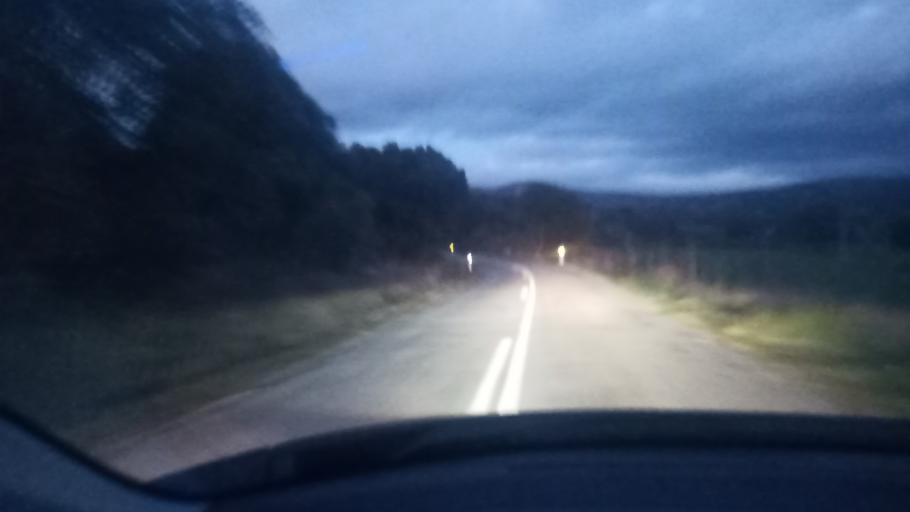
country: ES
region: Madrid
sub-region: Provincia de Madrid
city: Colmenar del Arroyo
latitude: 40.4427
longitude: -4.2398
